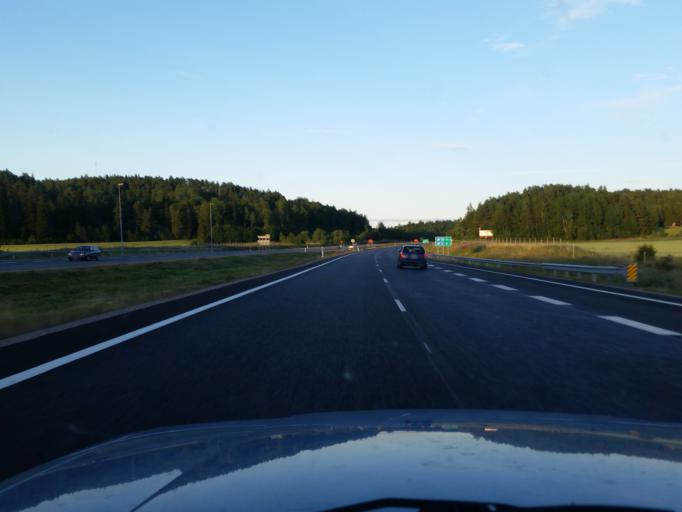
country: FI
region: Varsinais-Suomi
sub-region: Turku
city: Paimio
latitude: 60.4424
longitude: 22.6045
